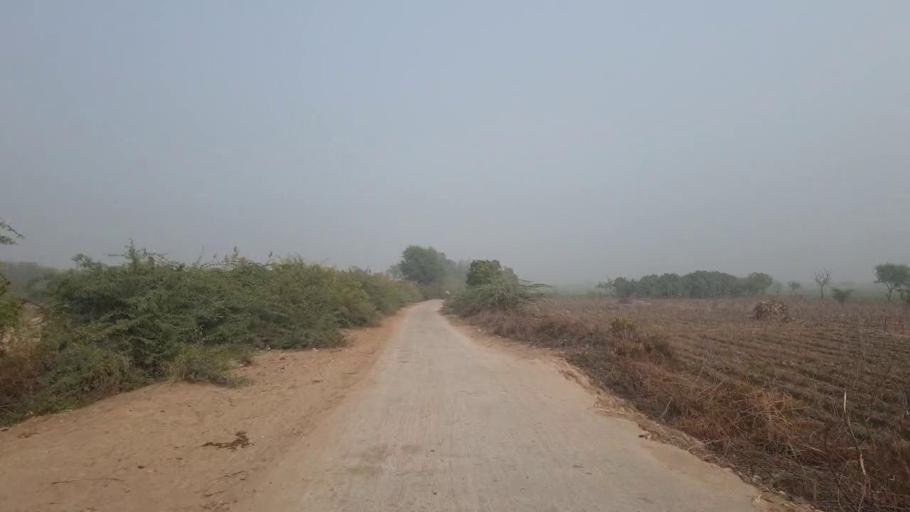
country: PK
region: Sindh
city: Bhit Shah
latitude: 25.8014
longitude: 68.5641
